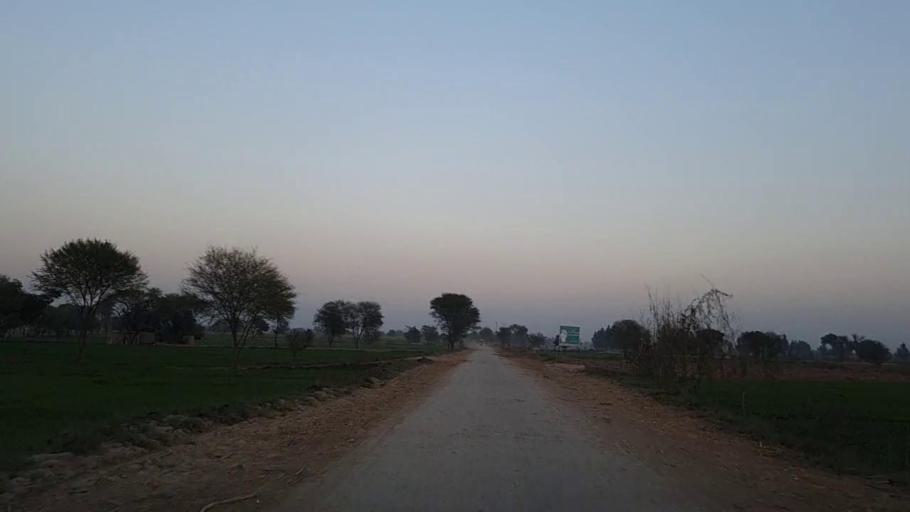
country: PK
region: Sindh
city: Naushahro Firoz
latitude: 26.8004
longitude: 68.0216
